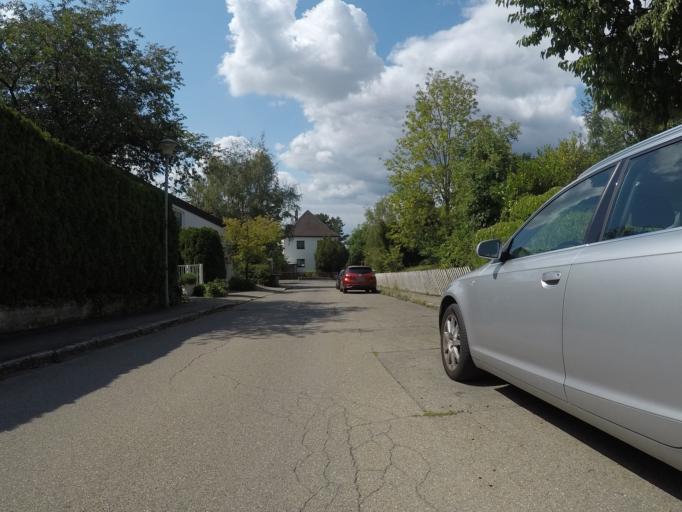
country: DE
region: Baden-Wuerttemberg
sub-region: Tuebingen Region
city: Reutlingen
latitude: 48.4898
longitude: 9.1948
